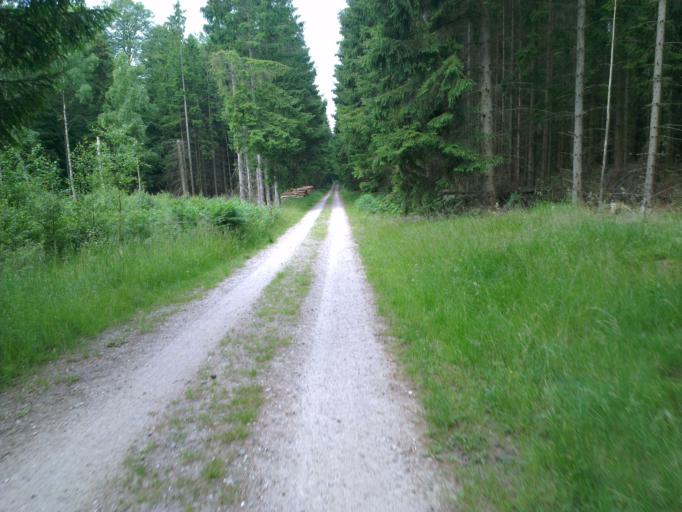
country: DK
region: Capital Region
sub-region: Allerod Kommune
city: Lillerod
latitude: 55.9135
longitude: 12.3494
